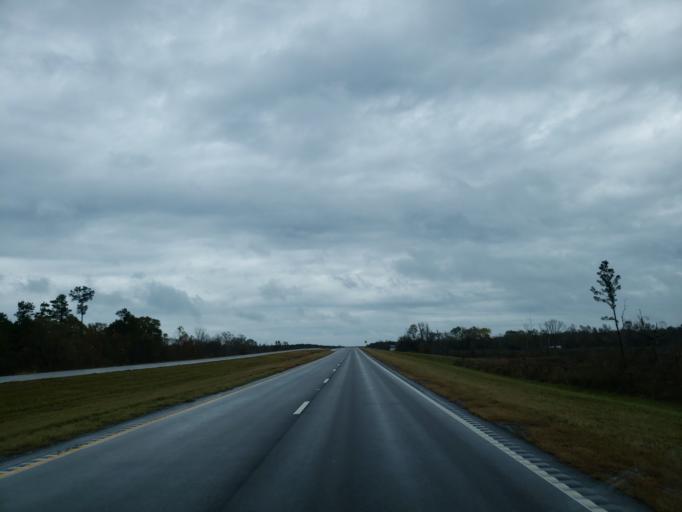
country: US
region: Mississippi
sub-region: Wayne County
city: Waynesboro
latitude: 31.6893
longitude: -88.6680
